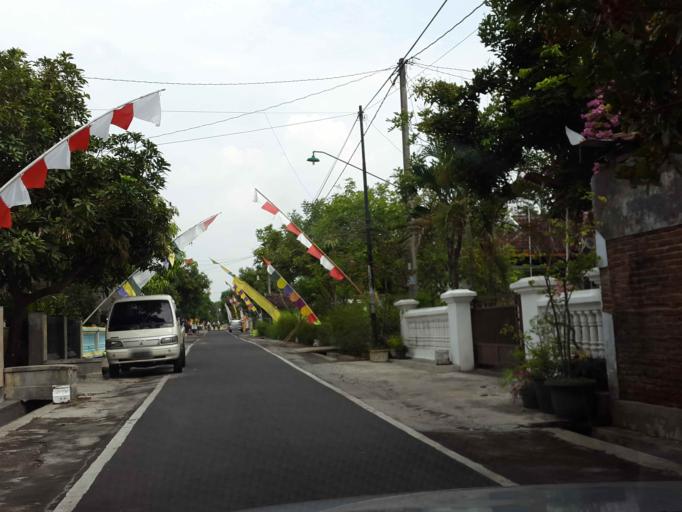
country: ID
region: Central Java
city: Jaten
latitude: -7.6011
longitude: 110.9599
